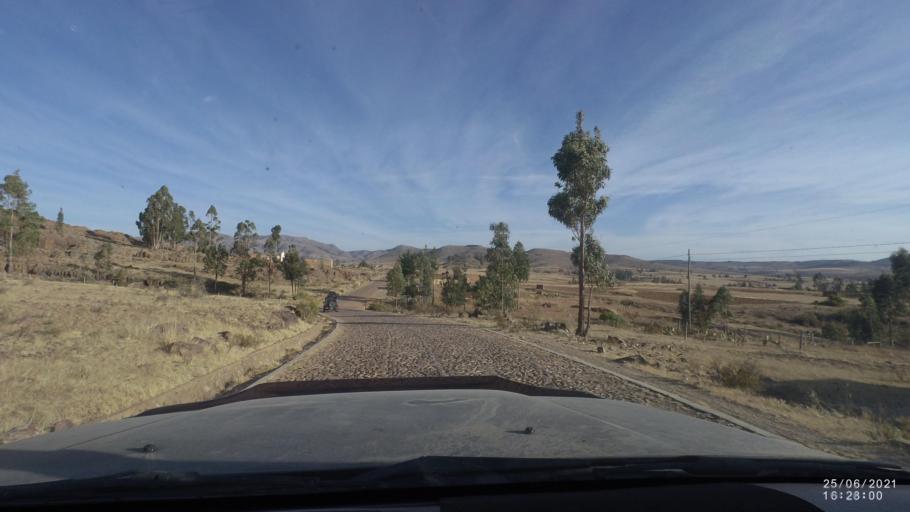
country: BO
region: Cochabamba
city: Arani
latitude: -17.7763
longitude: -65.8137
